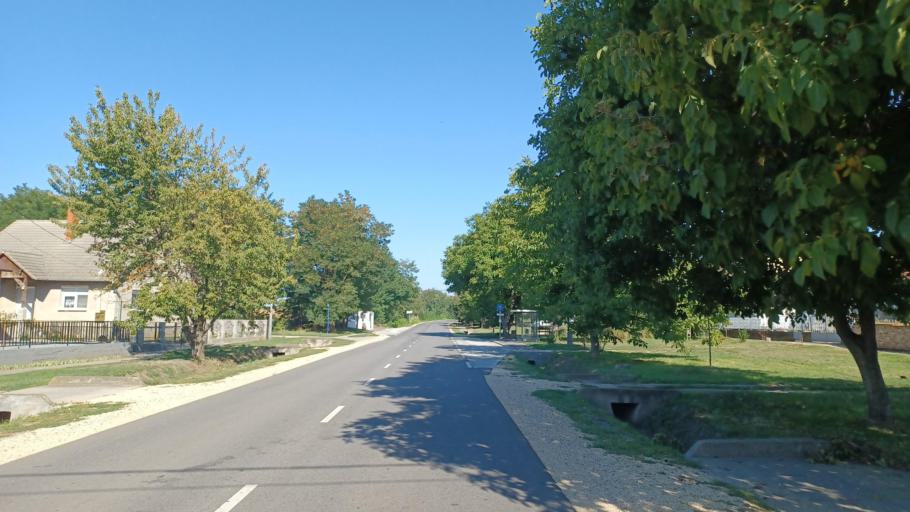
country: HU
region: Tolna
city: Nemetker
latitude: 46.6864
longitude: 18.8026
